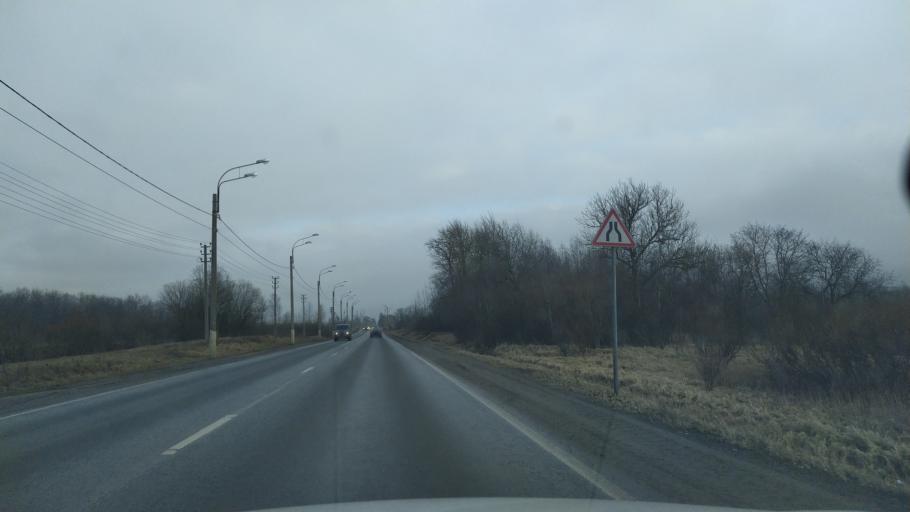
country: RU
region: St.-Petersburg
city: Aleksandrovskaya
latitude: 59.7131
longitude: 30.3063
